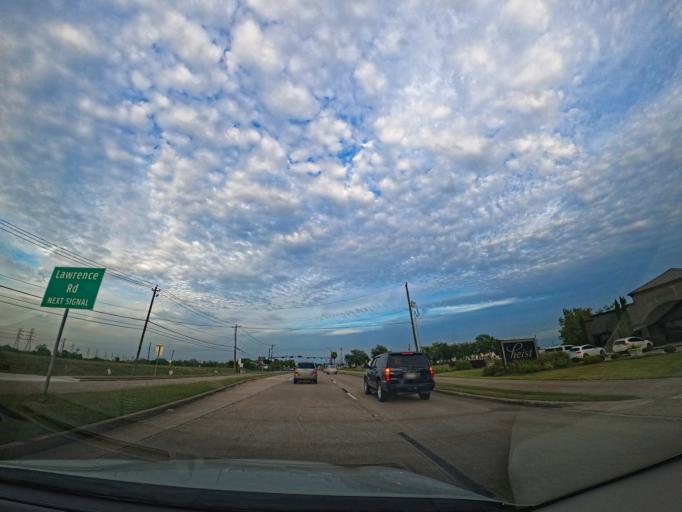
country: US
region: Texas
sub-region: Galveston County
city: Clear Lake Shores
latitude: 29.5294
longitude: -95.0346
